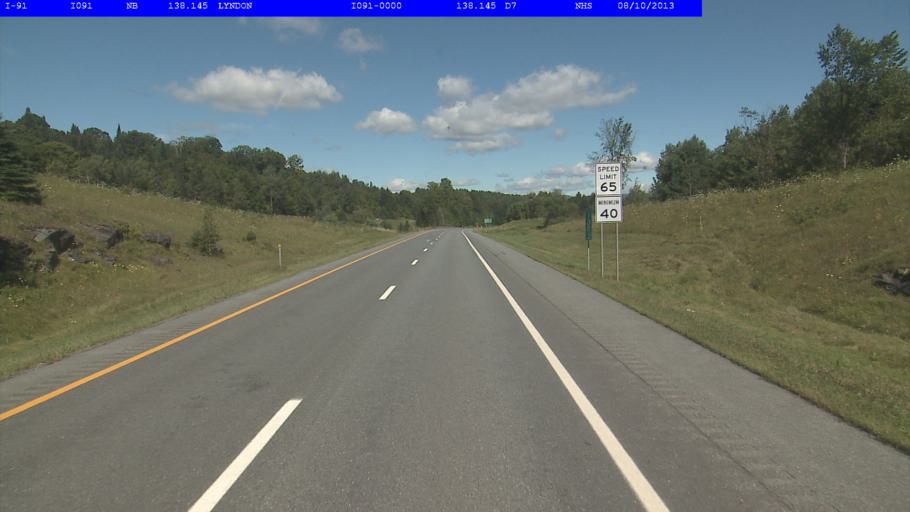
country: US
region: Vermont
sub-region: Caledonia County
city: Lyndonville
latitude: 44.5303
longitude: -72.0145
